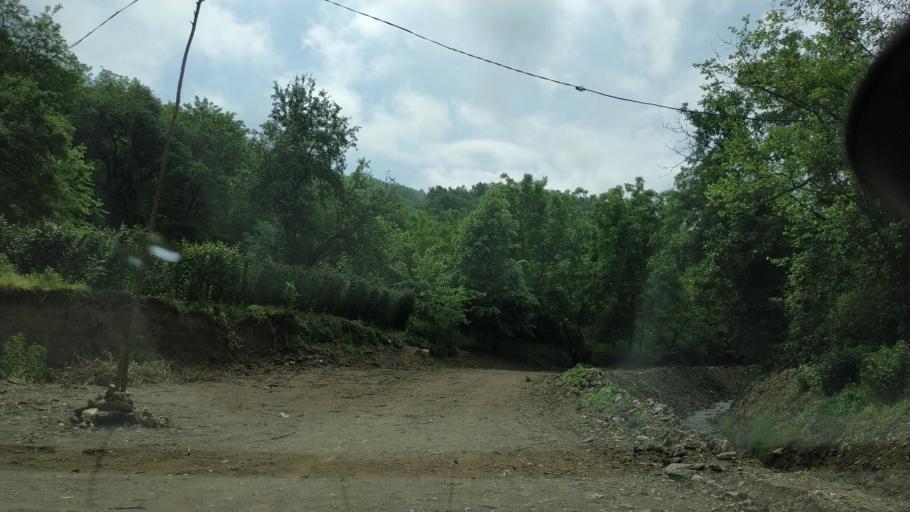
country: RS
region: Central Serbia
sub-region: Nisavski Okrug
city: Aleksinac
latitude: 43.4253
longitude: 21.6536
